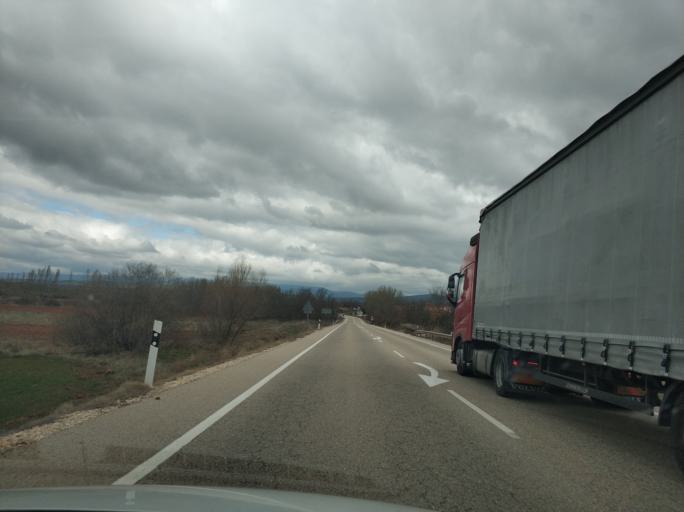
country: ES
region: Castille and Leon
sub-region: Provincia de Burgos
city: Hacinas
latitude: 41.9795
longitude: -3.2940
